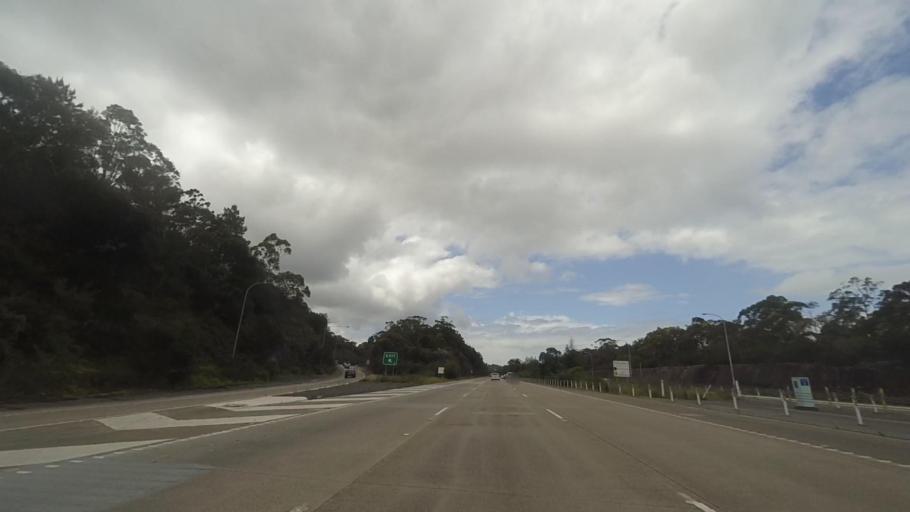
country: AU
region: New South Wales
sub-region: Gosford Shire
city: Point Clare
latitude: -33.4262
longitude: 151.2794
